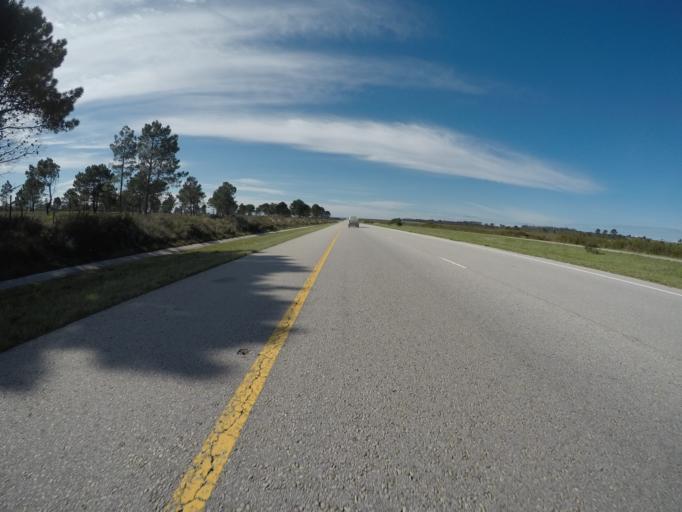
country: ZA
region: Eastern Cape
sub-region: Nelson Mandela Bay Metropolitan Municipality
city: Uitenhage
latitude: -33.9282
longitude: 25.3333
